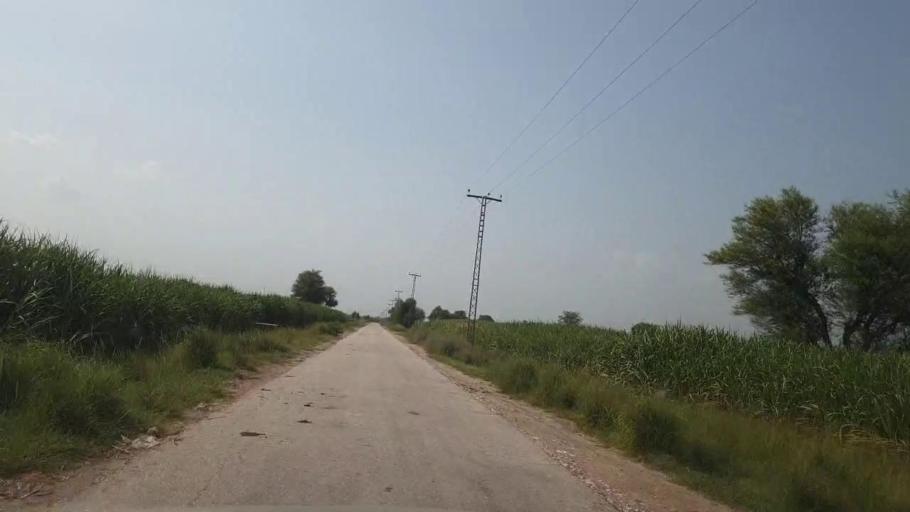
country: PK
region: Sindh
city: Pano Aqil
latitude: 27.7851
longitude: 69.1580
